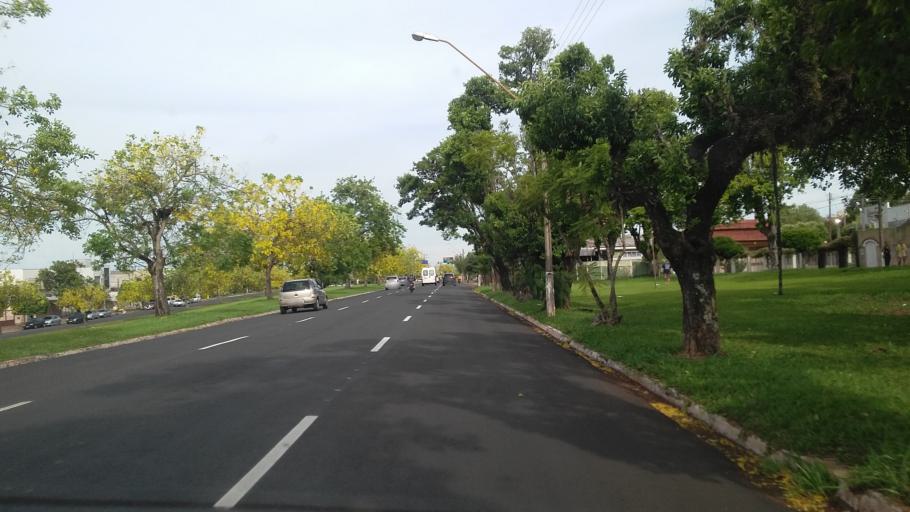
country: BR
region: Parana
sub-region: Londrina
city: Londrina
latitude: -23.2975
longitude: -51.1847
